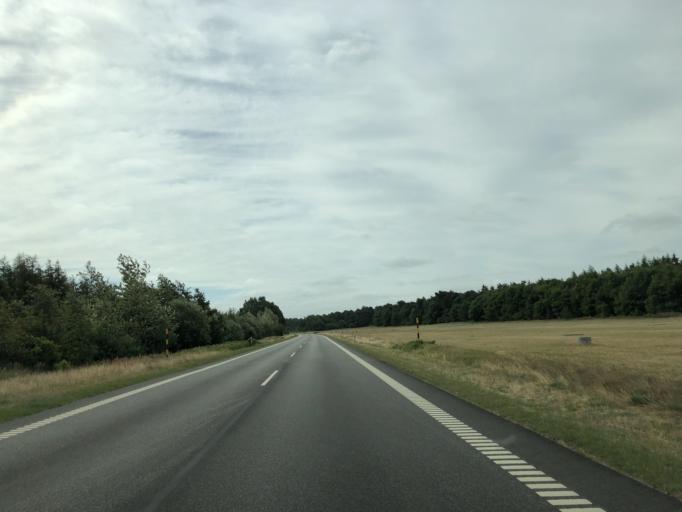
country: DK
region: Central Jutland
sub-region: Viborg Kommune
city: Karup
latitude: 56.3202
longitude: 9.1152
